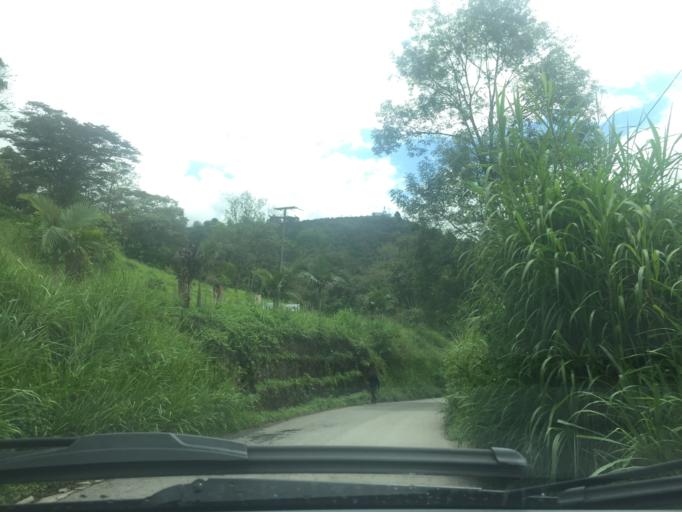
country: CO
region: Cundinamarca
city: San Francisco
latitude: 4.9855
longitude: -74.2883
